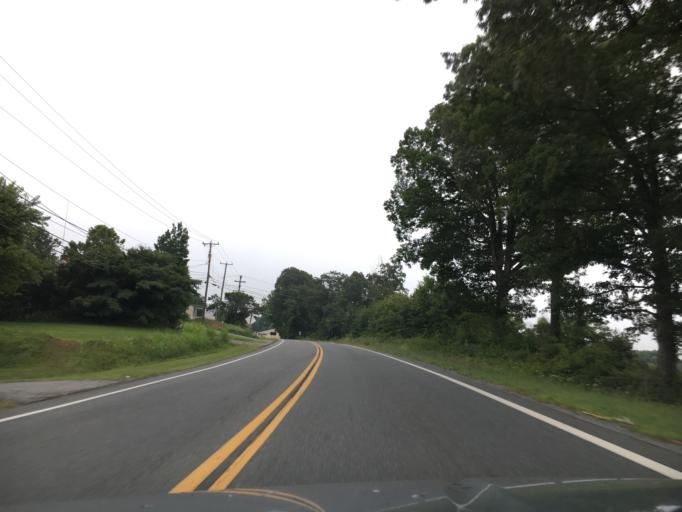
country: US
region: Virginia
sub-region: Campbell County
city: Brookneal
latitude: 37.0591
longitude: -78.9599
